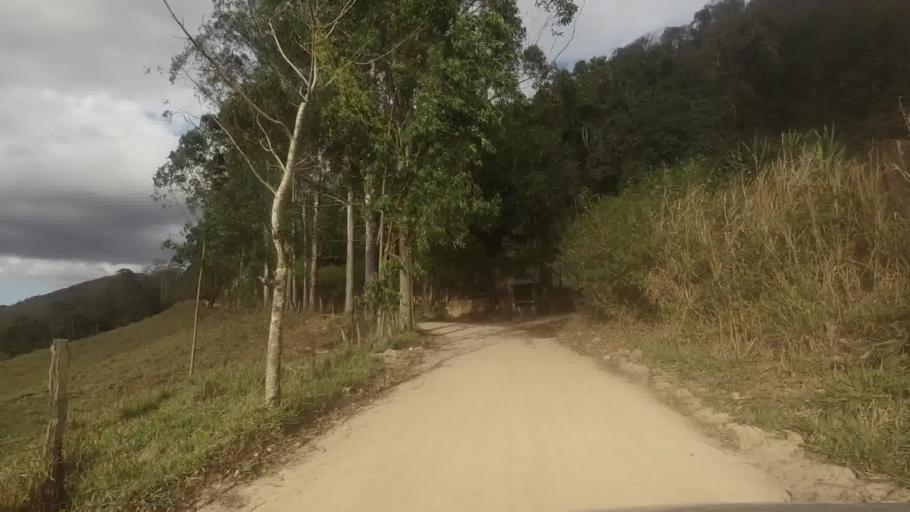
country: BR
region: Espirito Santo
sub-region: Mimoso Do Sul
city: Mimoso do Sul
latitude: -20.9678
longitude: -41.4501
